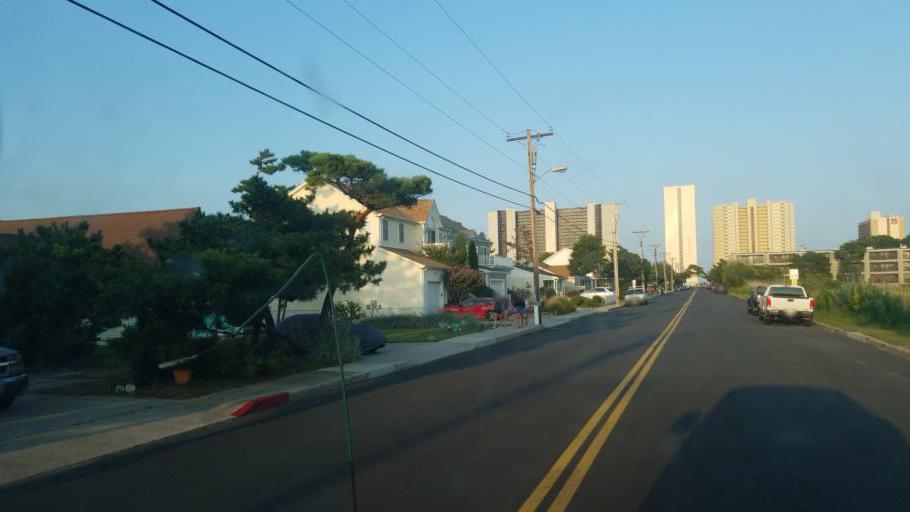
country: US
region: Maryland
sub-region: Worcester County
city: Ocean City
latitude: 38.4161
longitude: -75.0629
